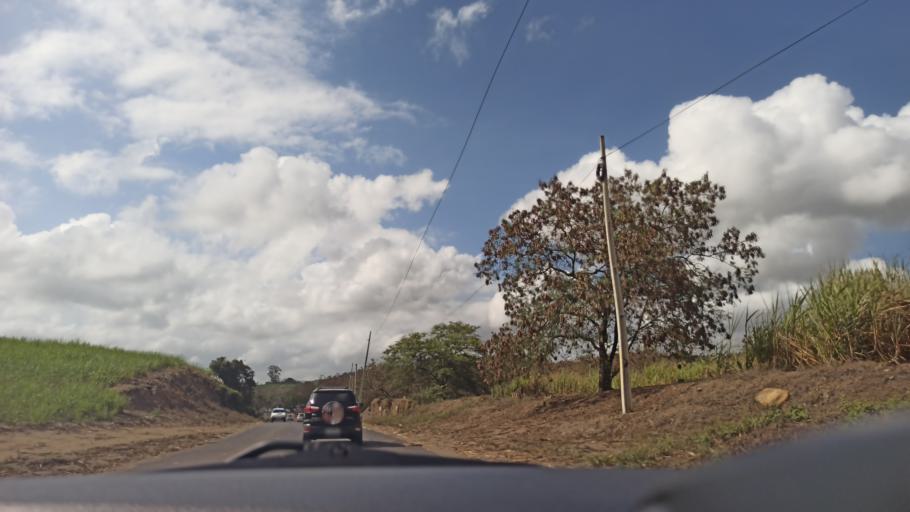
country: BR
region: Paraiba
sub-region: Juripiranga
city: Juripiranga
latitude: -7.4125
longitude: -35.2618
